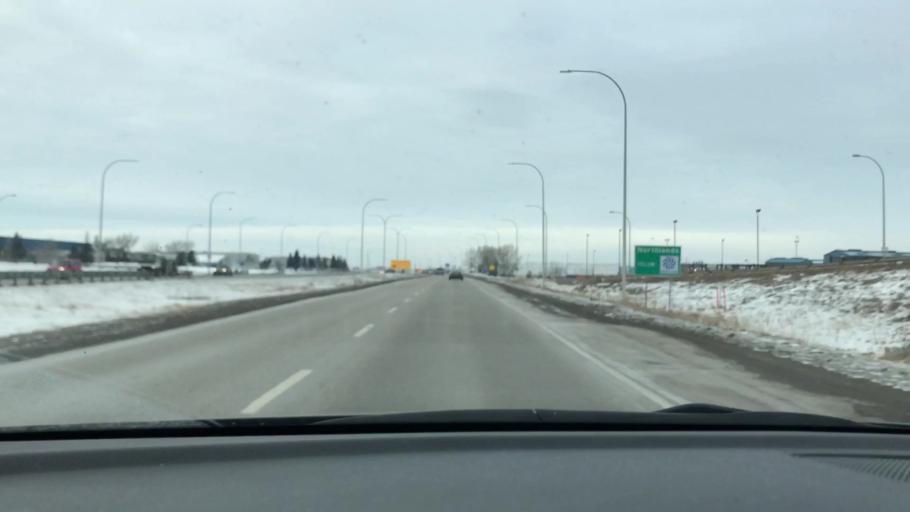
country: CA
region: Alberta
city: Sherwood Park
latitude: 53.5171
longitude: -113.3955
